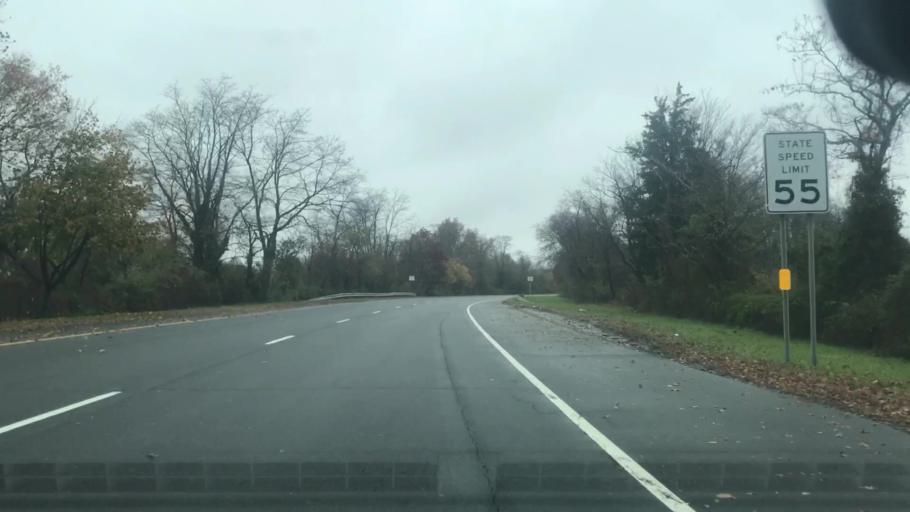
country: US
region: New York
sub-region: Suffolk County
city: Babylon
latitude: 40.6982
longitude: -73.3157
